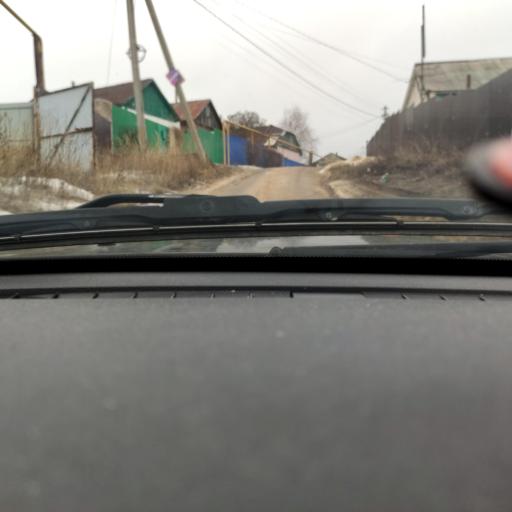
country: RU
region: Voronezj
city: Ramon'
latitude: 51.8173
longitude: 39.2724
